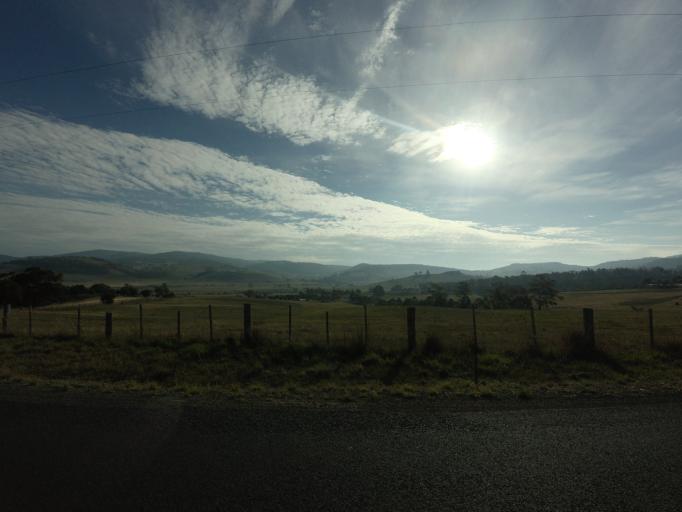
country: AU
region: Tasmania
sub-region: Brighton
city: Bridgewater
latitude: -42.5223
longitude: 147.3768
